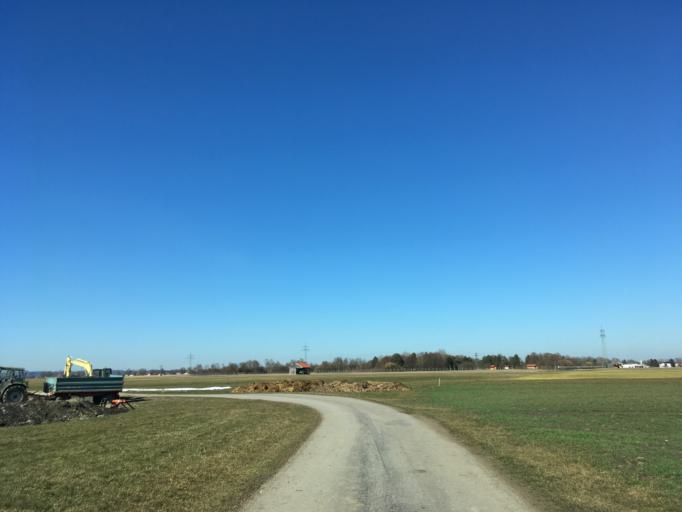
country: DE
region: Bavaria
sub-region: Upper Bavaria
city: Bad Aibling
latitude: 47.8414
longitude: 11.9922
